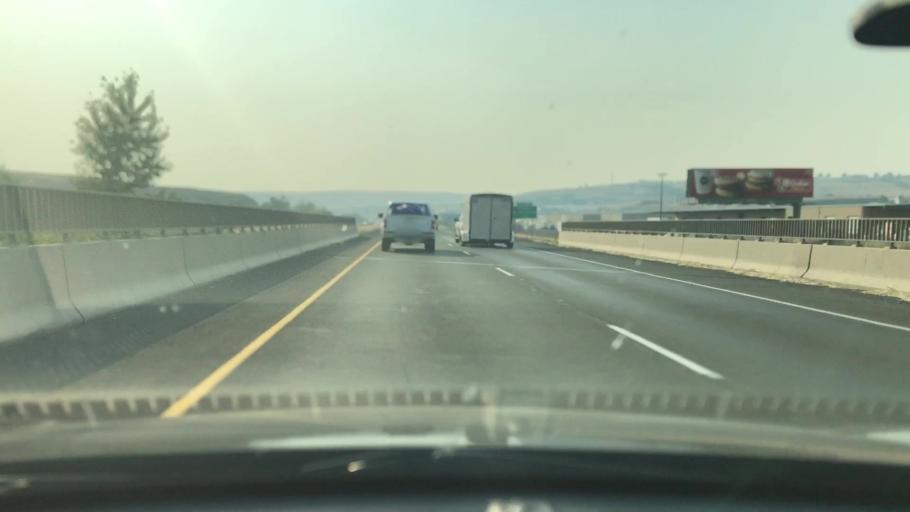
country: US
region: Oregon
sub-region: Umatilla County
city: Pendleton
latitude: 45.6665
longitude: -118.8175
